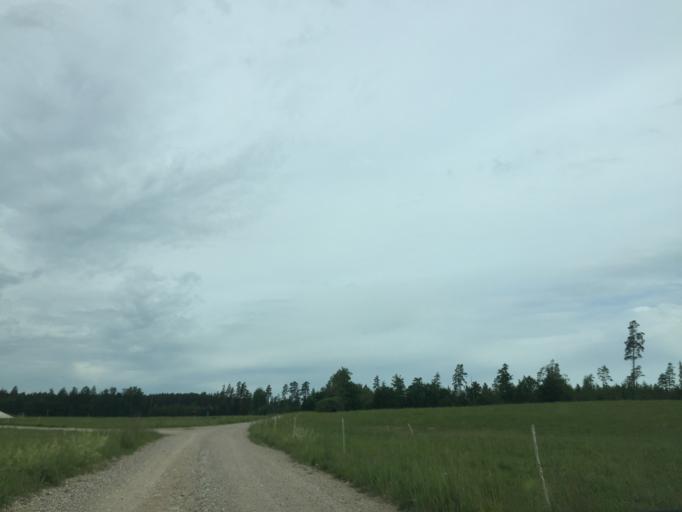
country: LV
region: Tukuma Rajons
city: Tukums
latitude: 57.0418
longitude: 23.1572
